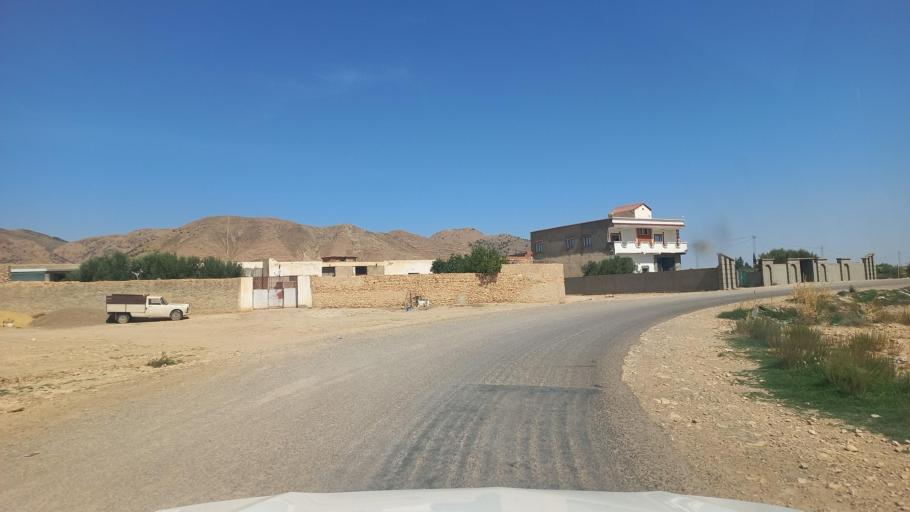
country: TN
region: Al Qasrayn
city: Sbiba
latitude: 35.4418
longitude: 9.0736
